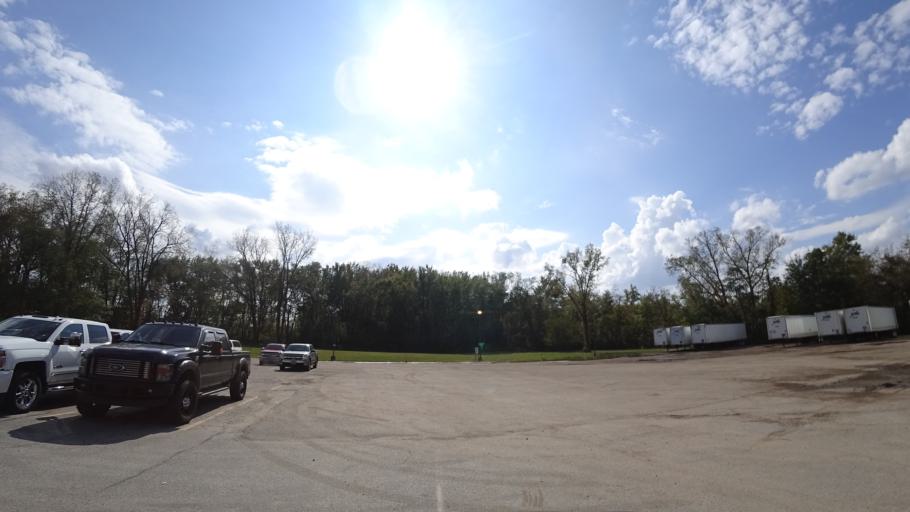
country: US
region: Michigan
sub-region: Saint Joseph County
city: Three Rivers
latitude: 41.9284
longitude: -85.6317
